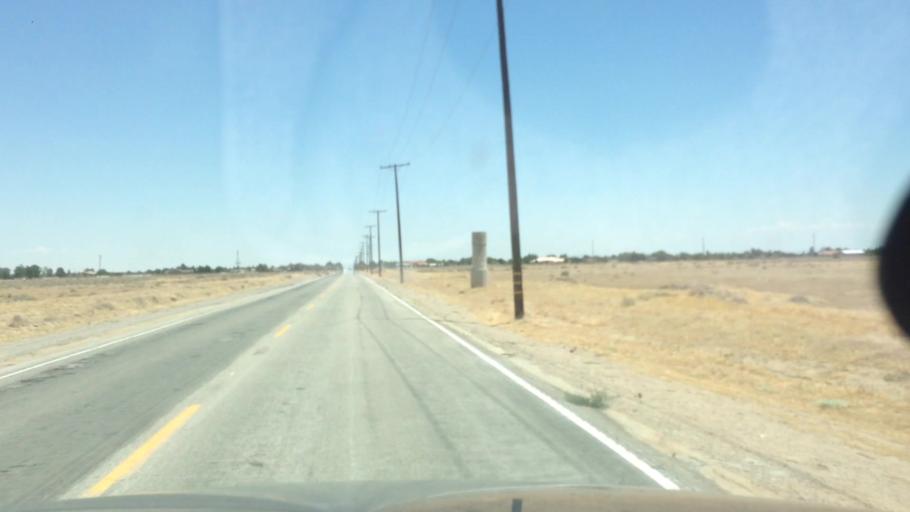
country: US
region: California
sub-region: Los Angeles County
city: Quartz Hill
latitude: 34.7764
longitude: -118.2977
